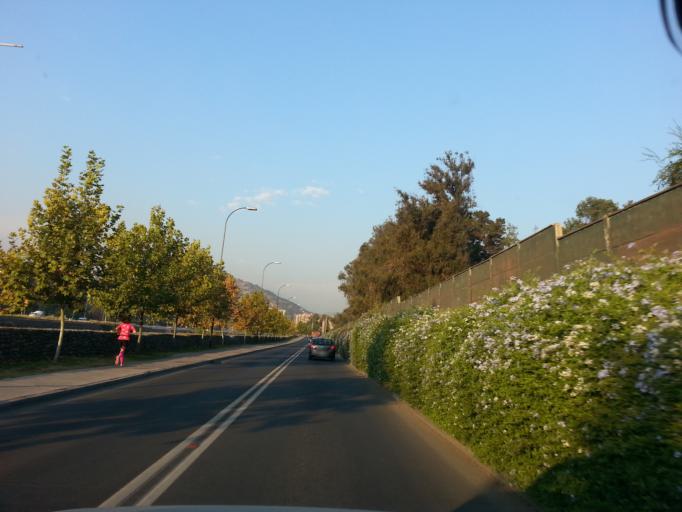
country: CL
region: Santiago Metropolitan
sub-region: Provincia de Santiago
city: Villa Presidente Frei, Nunoa, Santiago, Chile
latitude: -33.3774
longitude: -70.5610
